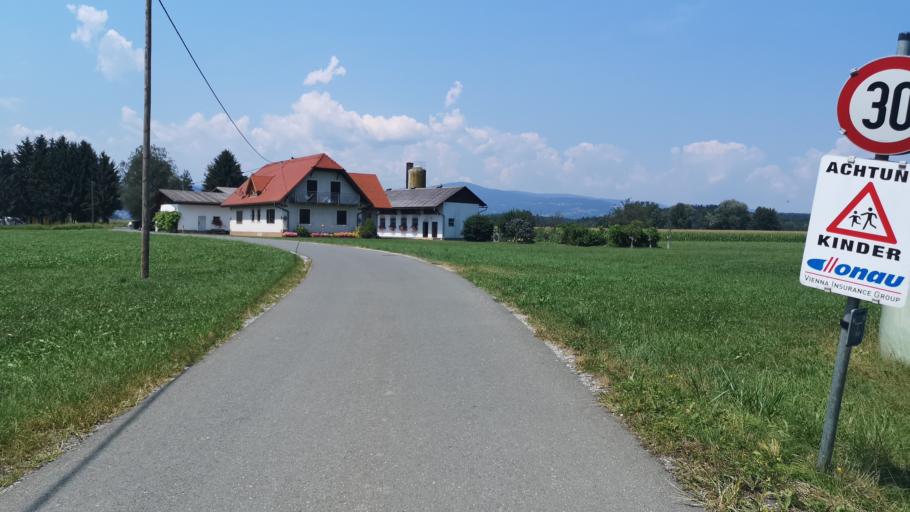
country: AT
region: Styria
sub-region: Politischer Bezirk Deutschlandsberg
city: Gross Sankt Florian
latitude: 46.8169
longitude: 15.3018
